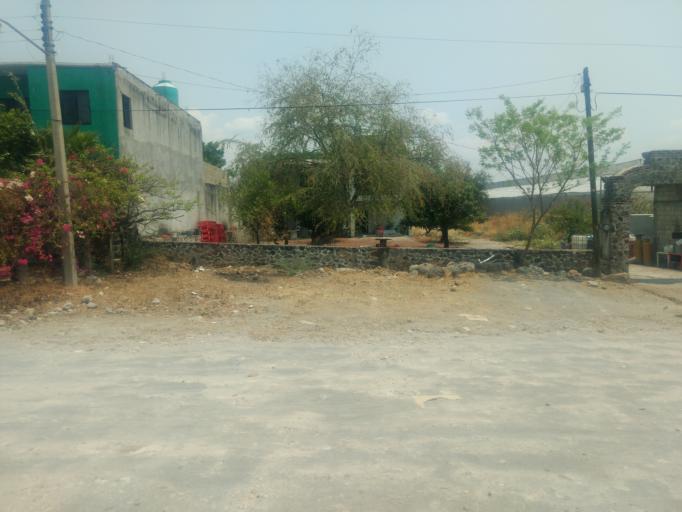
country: MX
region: Morelos
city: La Joya
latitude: 18.7008
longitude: -99.4754
